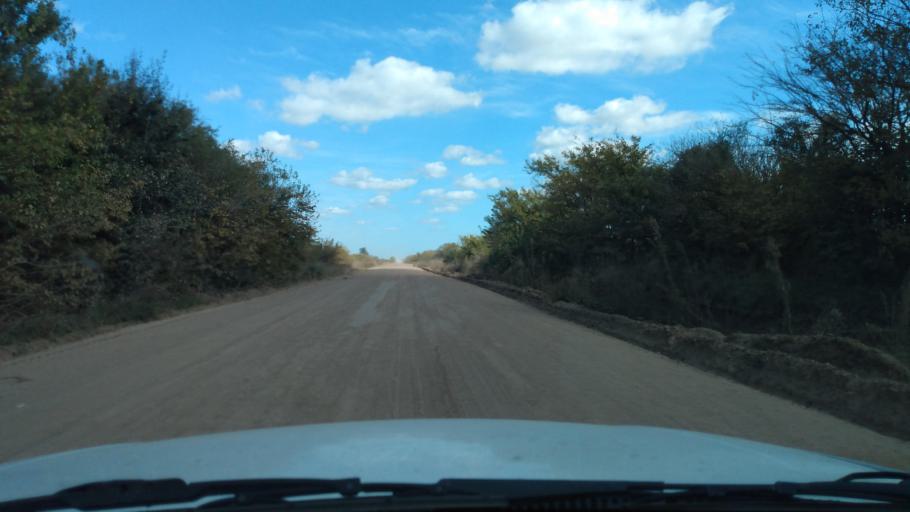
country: AR
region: Buenos Aires
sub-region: Partido de Navarro
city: Navarro
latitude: -35.0313
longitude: -59.4516
